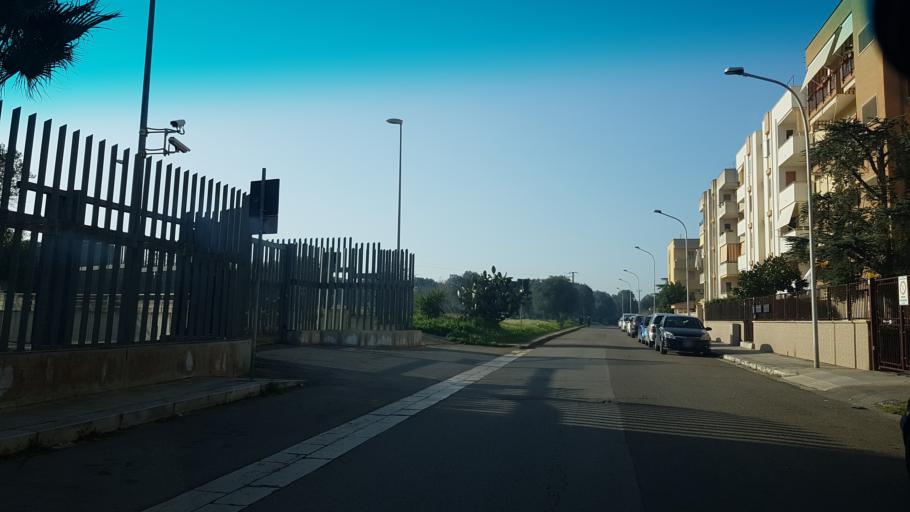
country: IT
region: Apulia
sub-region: Provincia di Brindisi
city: San Vito dei Normanni
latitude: 40.6630
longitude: 17.6950
